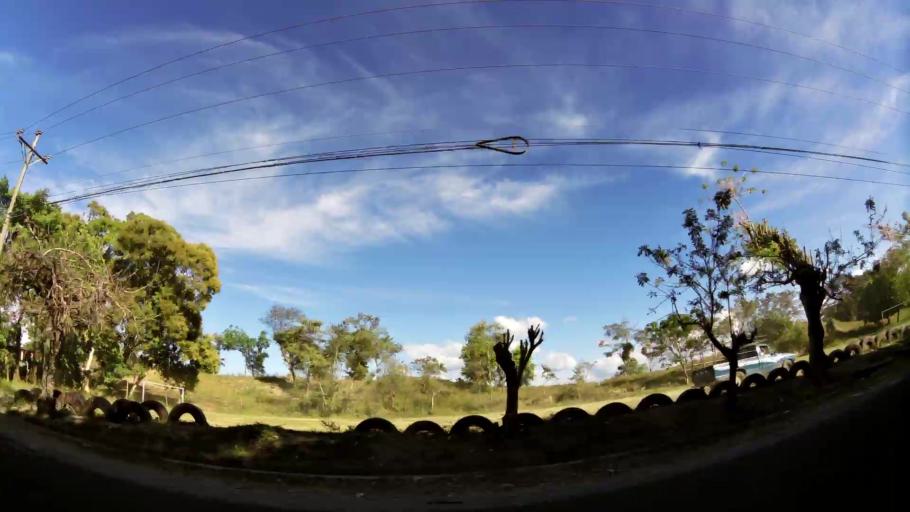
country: SV
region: Cuscatlan
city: Tecoluca
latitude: 13.8074
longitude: -89.0352
